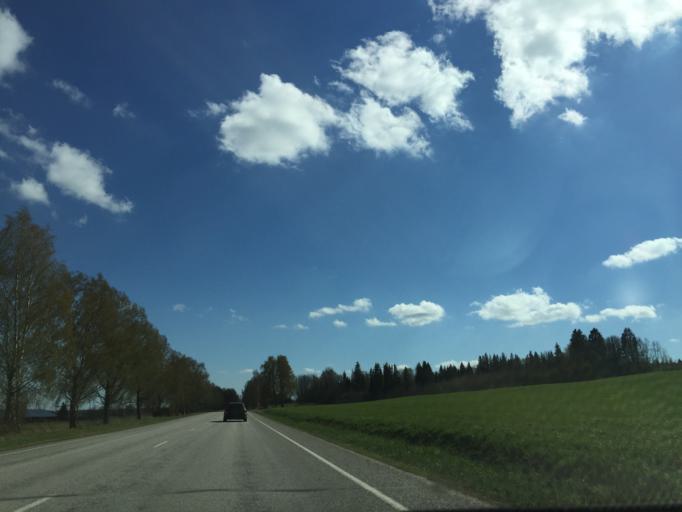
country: EE
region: Valgamaa
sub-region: Valga linn
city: Valga
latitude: 57.8926
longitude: 26.0546
